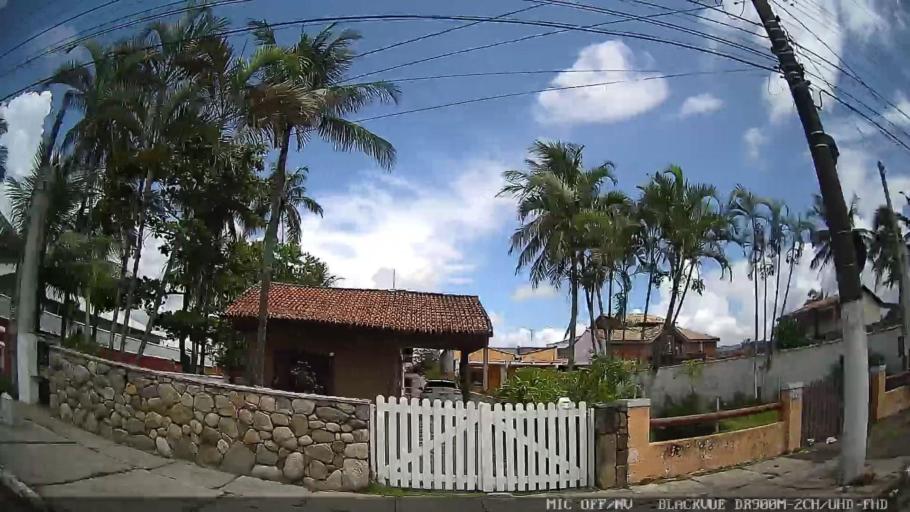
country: BR
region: Sao Paulo
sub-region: Caraguatatuba
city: Caraguatatuba
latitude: -23.6690
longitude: -45.4316
